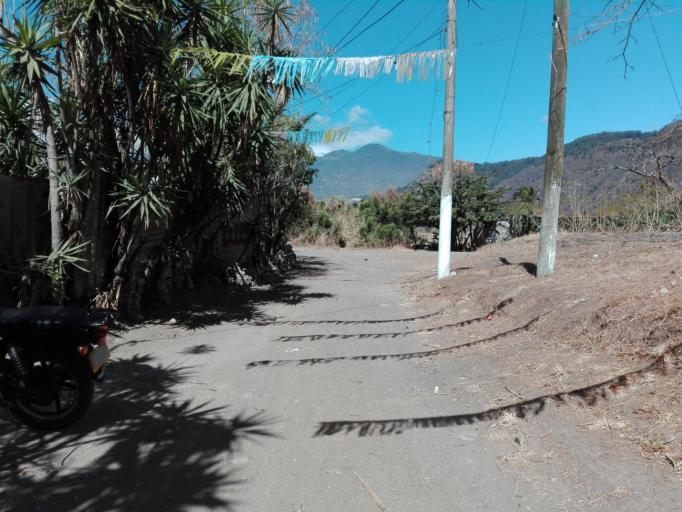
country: GT
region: Guatemala
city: Amatitlan
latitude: 14.4771
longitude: -90.5955
